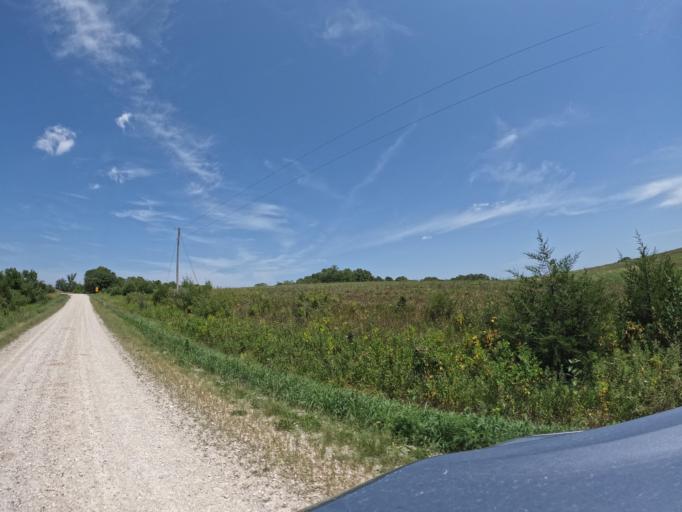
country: US
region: Iowa
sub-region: Henry County
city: Mount Pleasant
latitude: 40.9183
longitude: -91.6652
